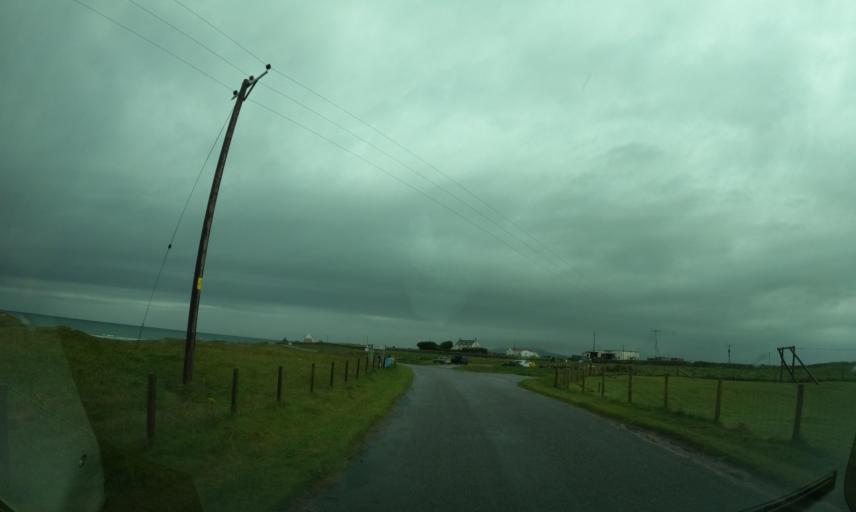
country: GB
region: Scotland
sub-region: Eilean Siar
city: Barra
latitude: 56.4893
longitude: -6.8791
